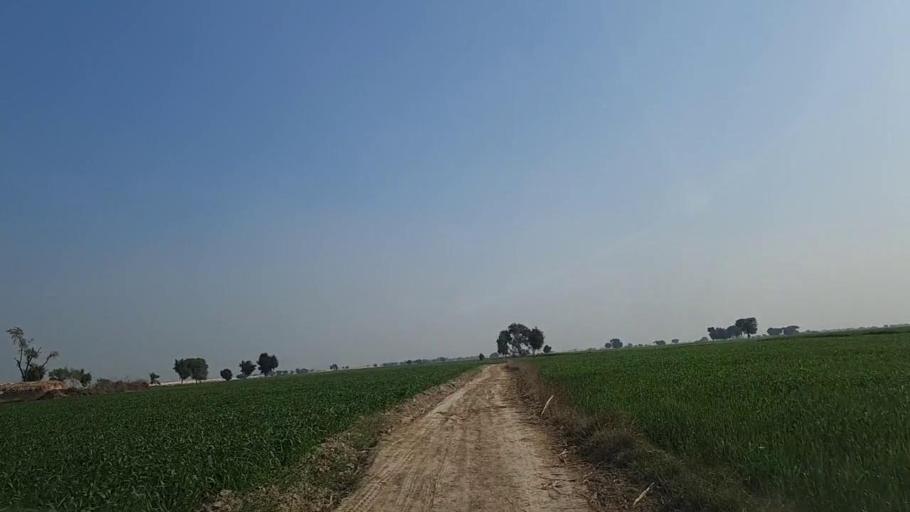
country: PK
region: Sindh
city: Moro
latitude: 26.6814
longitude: 67.9353
